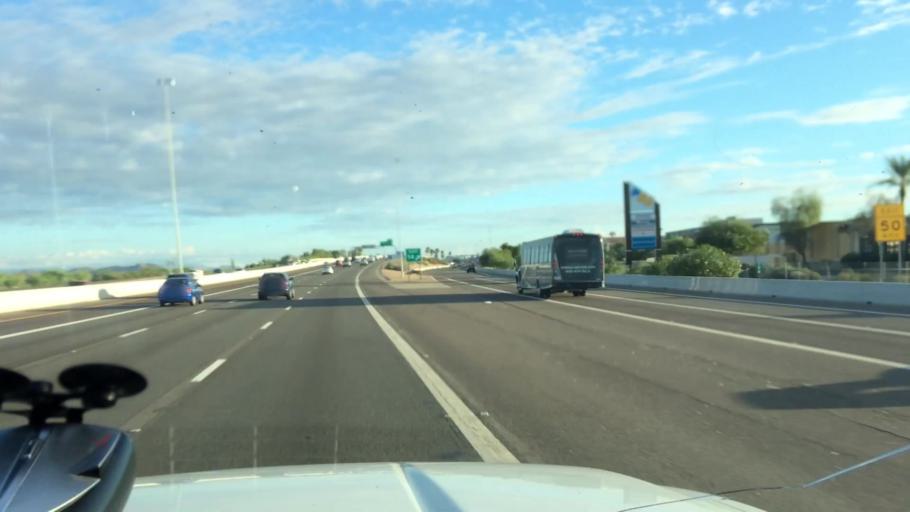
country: US
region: Arizona
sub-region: Maricopa County
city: Sun City
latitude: 33.6322
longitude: -112.2392
